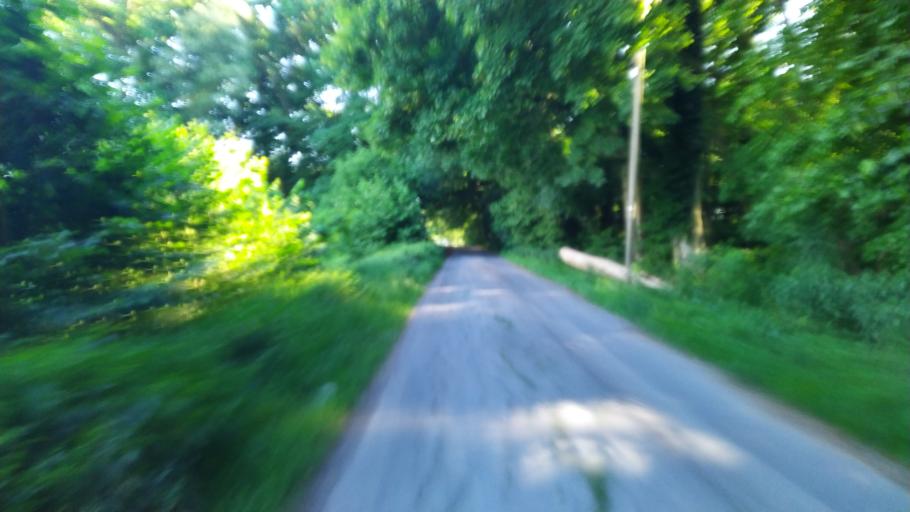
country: DE
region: Lower Saxony
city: Lintig
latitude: 53.5953
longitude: 8.9296
